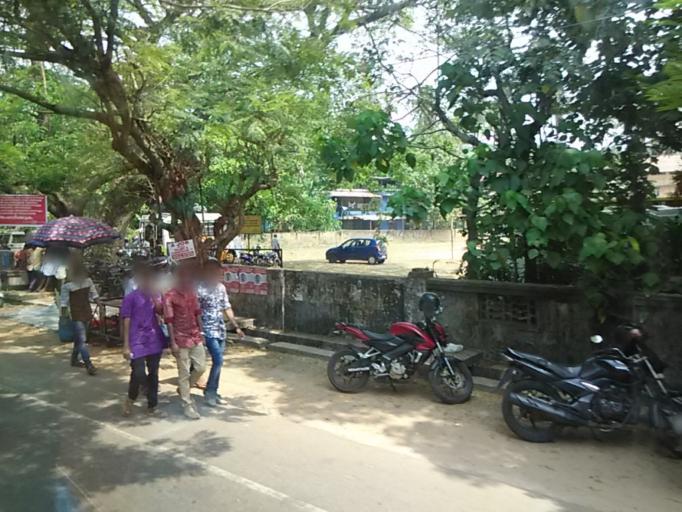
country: IN
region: Kerala
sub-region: Kozhikode
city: Kozhikode
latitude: 11.2870
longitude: 75.7676
